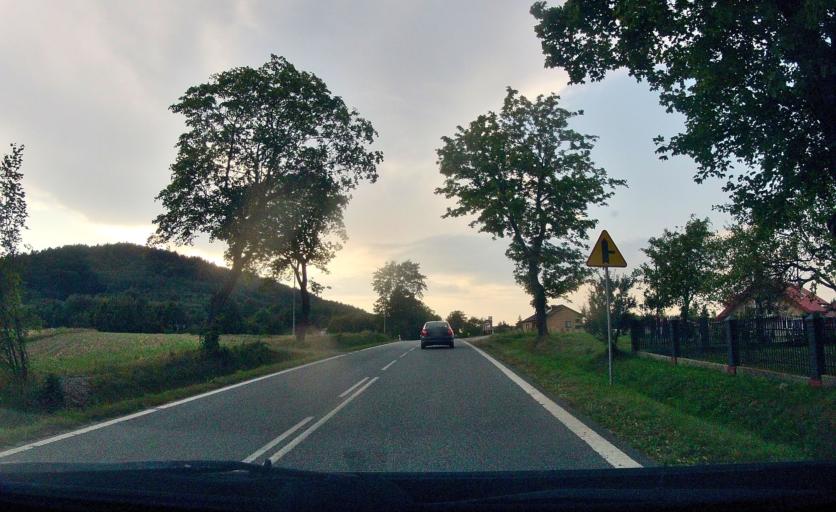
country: PL
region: Subcarpathian Voivodeship
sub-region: Powiat jasielski
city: Nowy Zmigrod
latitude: 49.5698
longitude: 21.5743
